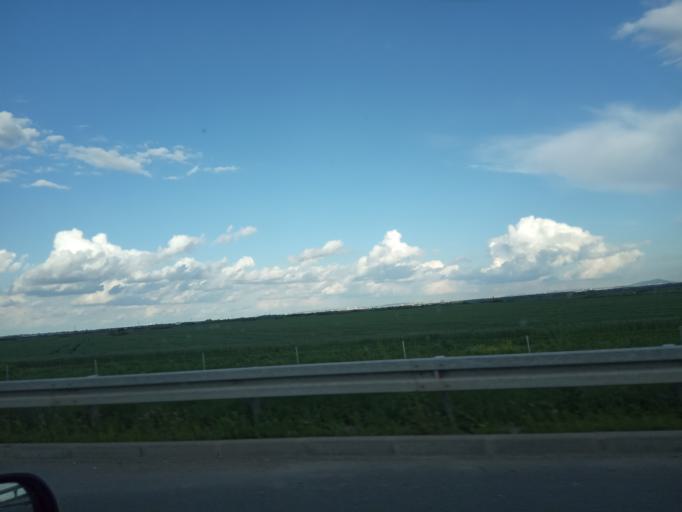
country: RS
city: Dobanovci
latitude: 44.8690
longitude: 20.2579
